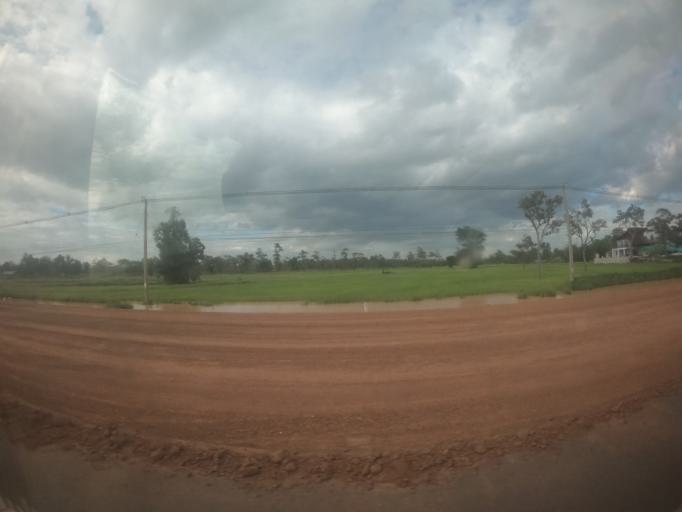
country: TH
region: Surin
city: Kap Choeng
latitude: 14.5103
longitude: 103.5530
